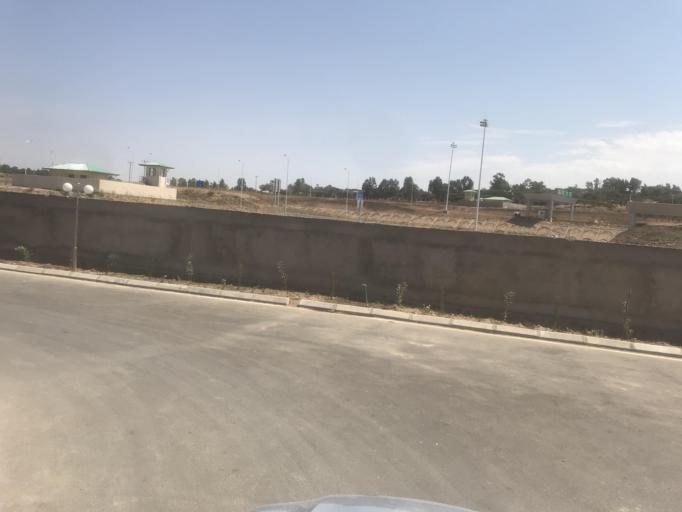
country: ET
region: Oromiya
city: Mojo
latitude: 8.5674
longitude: 39.1623
